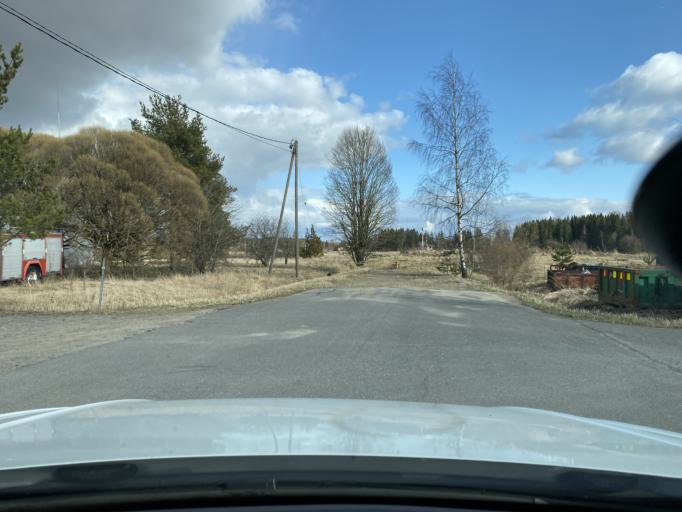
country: FI
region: Pirkanmaa
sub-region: Lounais-Pirkanmaa
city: Punkalaidun
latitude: 61.1192
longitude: 23.0936
